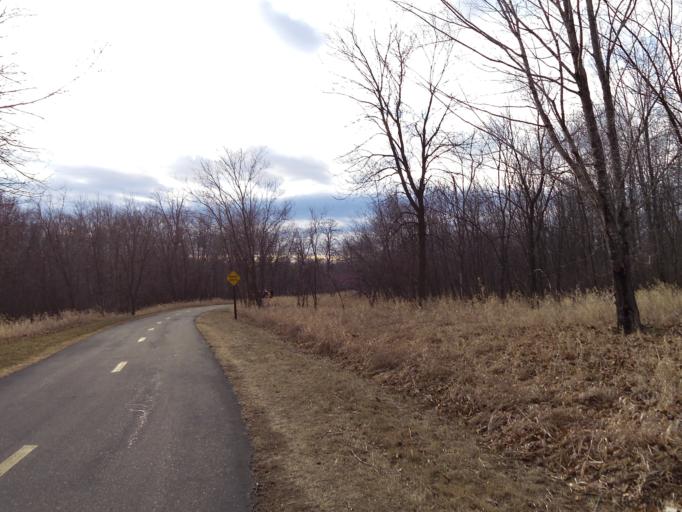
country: US
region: Minnesota
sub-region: Scott County
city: Prior Lake
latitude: 44.6957
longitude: -93.3877
